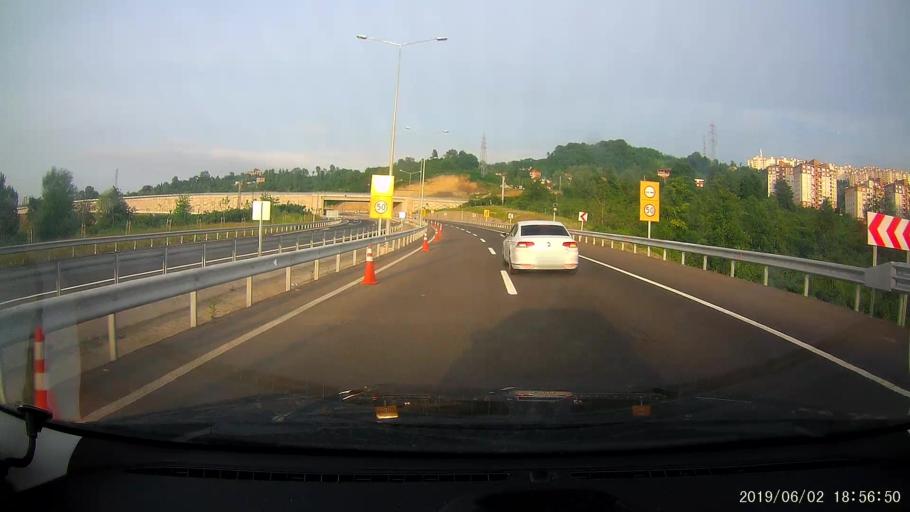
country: TR
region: Ordu
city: Ordu
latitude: 40.9536
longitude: 37.9001
